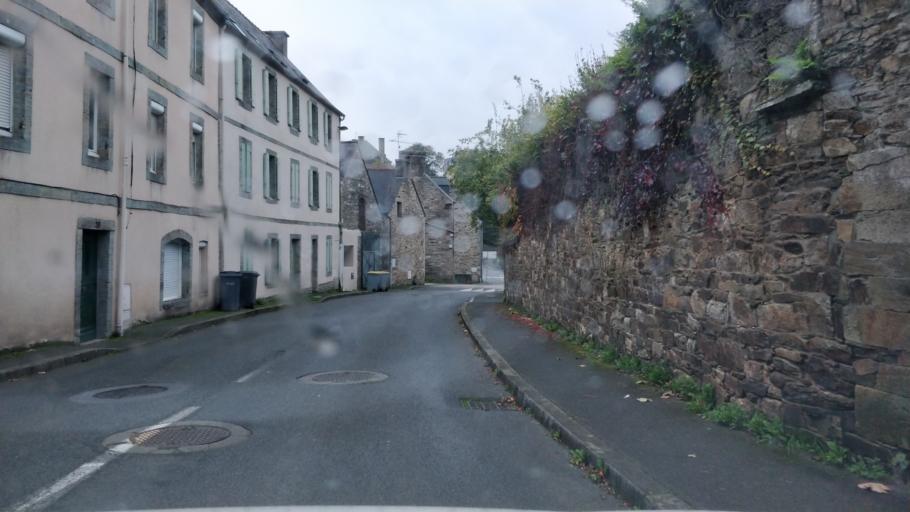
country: FR
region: Brittany
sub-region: Departement des Cotes-d'Armor
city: Lannion
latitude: 48.7361
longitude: -3.4550
